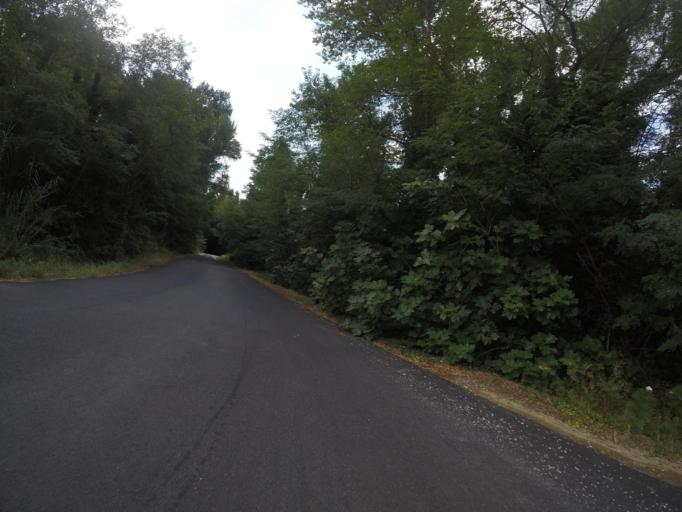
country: FR
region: Languedoc-Roussillon
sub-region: Departement des Pyrenees-Orientales
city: Ille-sur-Tet
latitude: 42.6933
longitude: 2.6535
